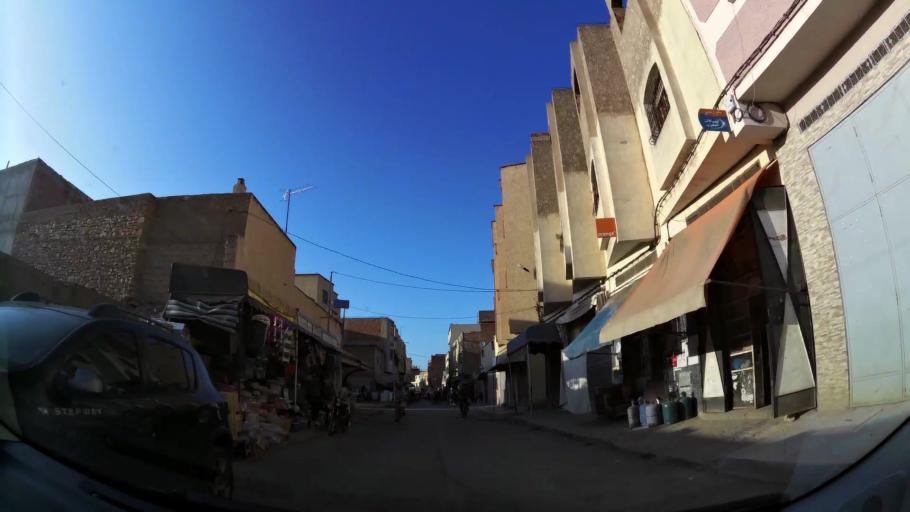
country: MA
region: Oriental
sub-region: Oujda-Angad
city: Oujda
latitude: 34.7033
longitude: -1.9102
